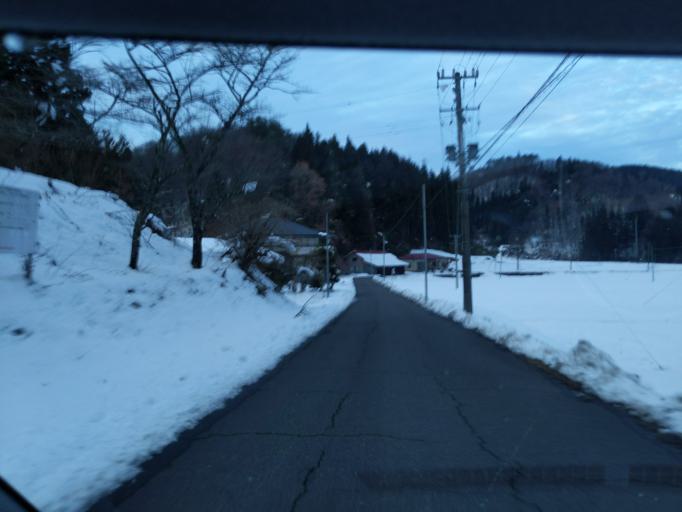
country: JP
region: Iwate
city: Mizusawa
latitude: 39.0448
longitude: 141.0122
